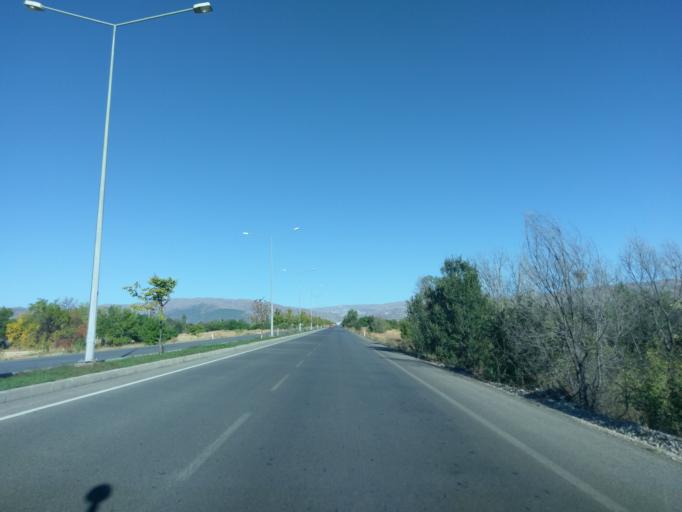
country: TR
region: Erzincan
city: Erzincan
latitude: 39.7776
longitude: 39.4138
